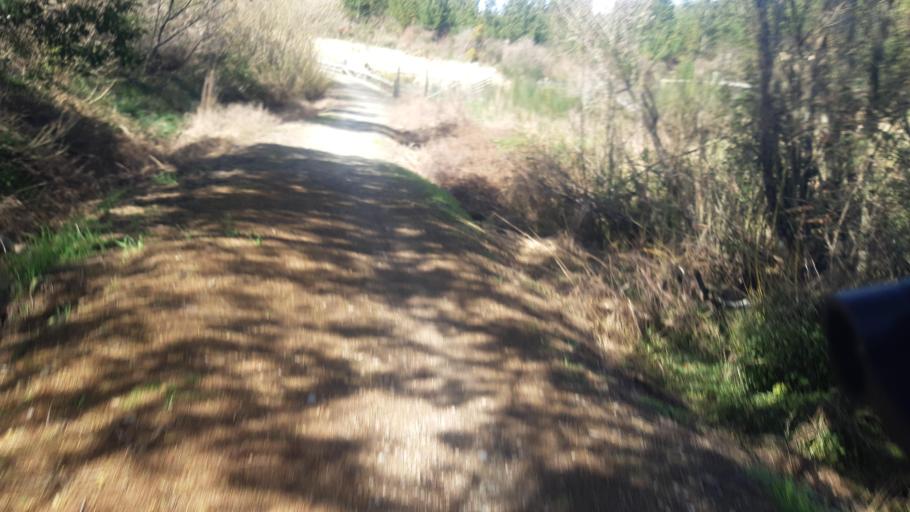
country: NZ
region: Tasman
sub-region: Tasman District
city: Wakefield
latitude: -41.4425
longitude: 172.9809
